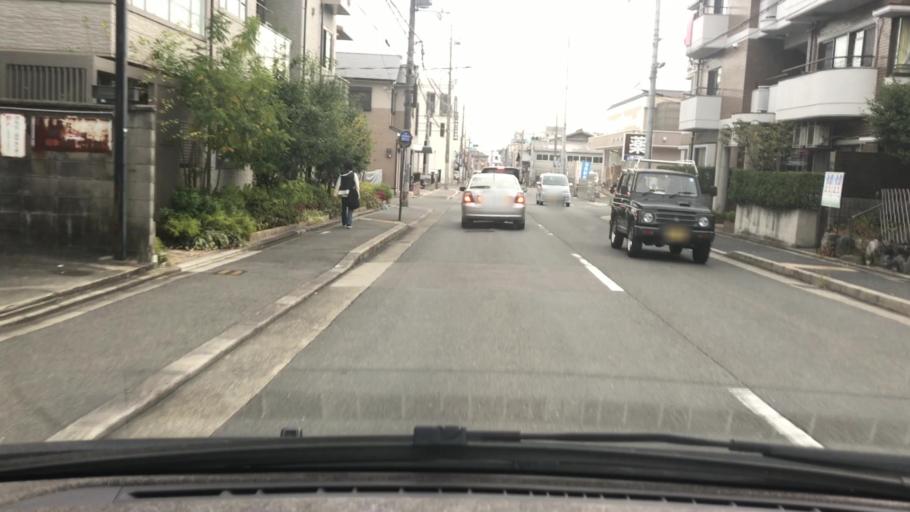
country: JP
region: Kyoto
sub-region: Kyoto-shi
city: Kamigyo-ku
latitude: 35.0501
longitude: 135.7441
